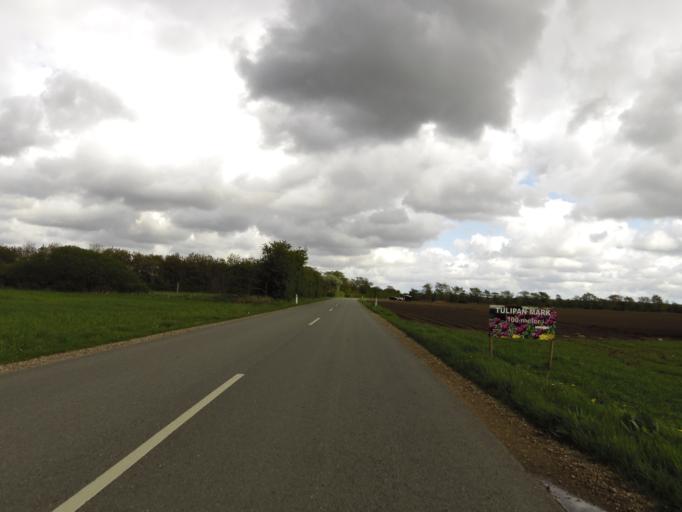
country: DK
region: South Denmark
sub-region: Haderslev Kommune
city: Gram
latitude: 55.3043
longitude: 9.0072
